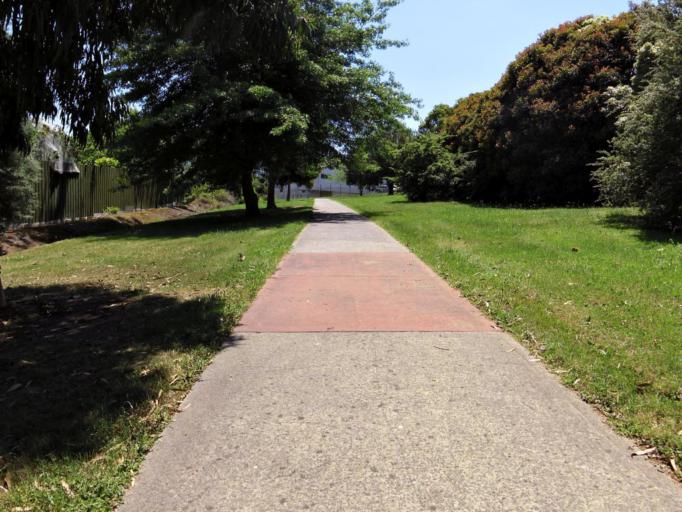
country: AU
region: Victoria
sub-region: Casey
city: Endeavour Hills
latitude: -37.9797
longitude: 145.2613
